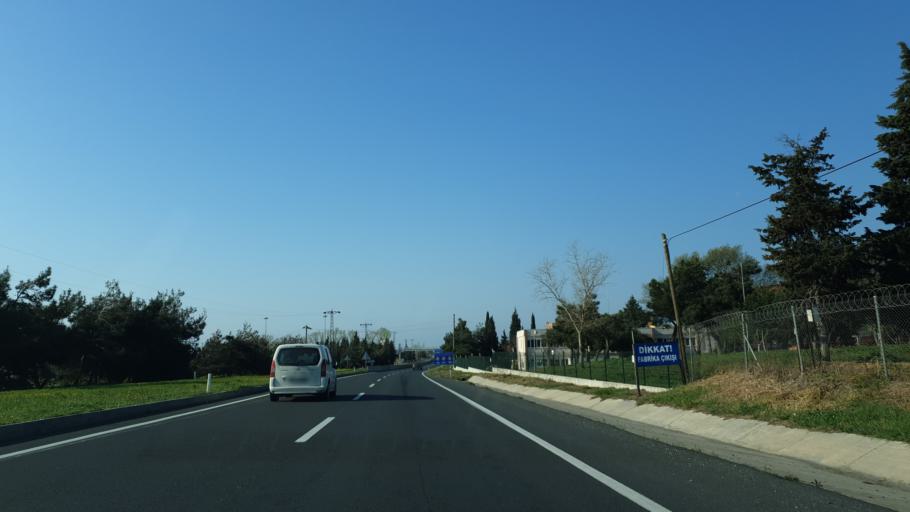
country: TR
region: Tekirdag
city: Corlu
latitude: 41.0229
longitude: 27.7230
